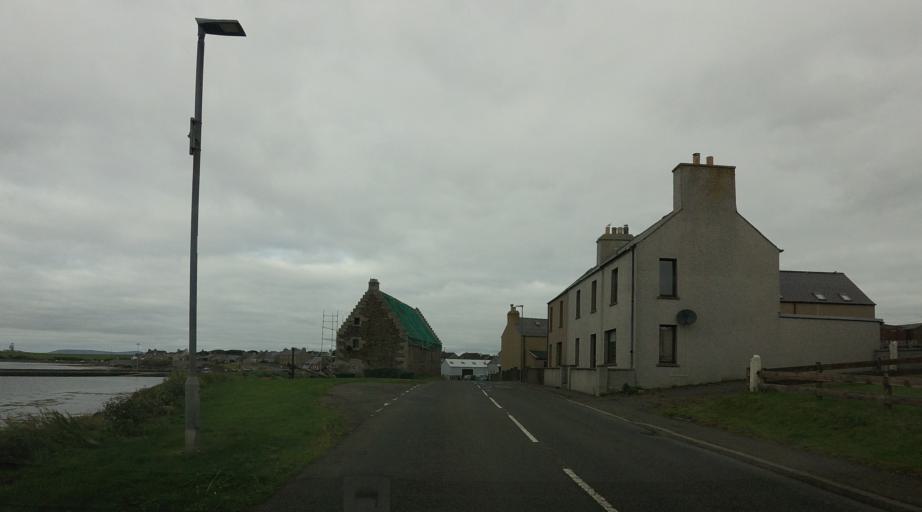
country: GB
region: Scotland
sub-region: Orkney Islands
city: Kirkwall
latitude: 58.8959
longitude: -2.9081
